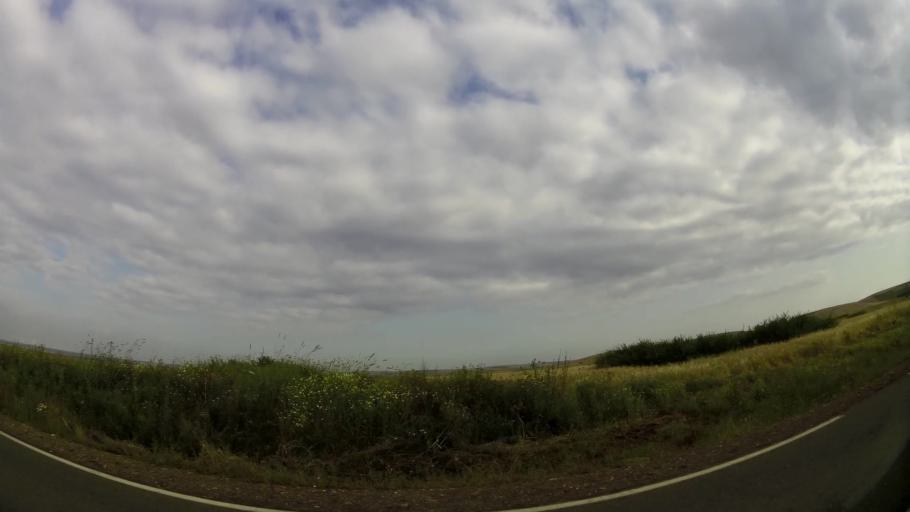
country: MA
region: Rabat-Sale-Zemmour-Zaer
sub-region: Khemisset
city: Khemisset
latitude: 33.7683
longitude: -6.1658
